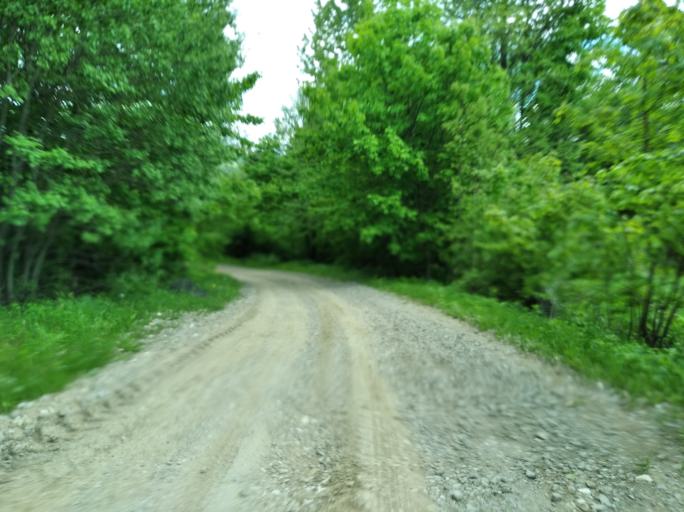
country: PL
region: Subcarpathian Voivodeship
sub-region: Powiat strzyzowski
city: Frysztak
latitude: 49.8330
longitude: 21.5515
